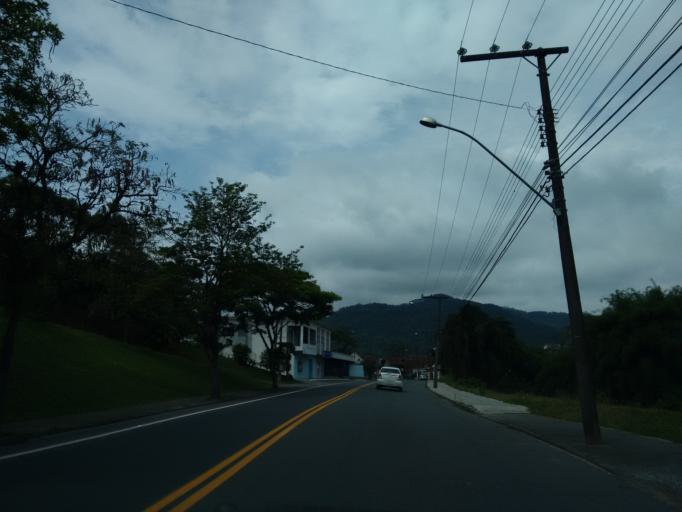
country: BR
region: Santa Catarina
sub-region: Pomerode
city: Pomerode
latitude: -26.7228
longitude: -49.1686
